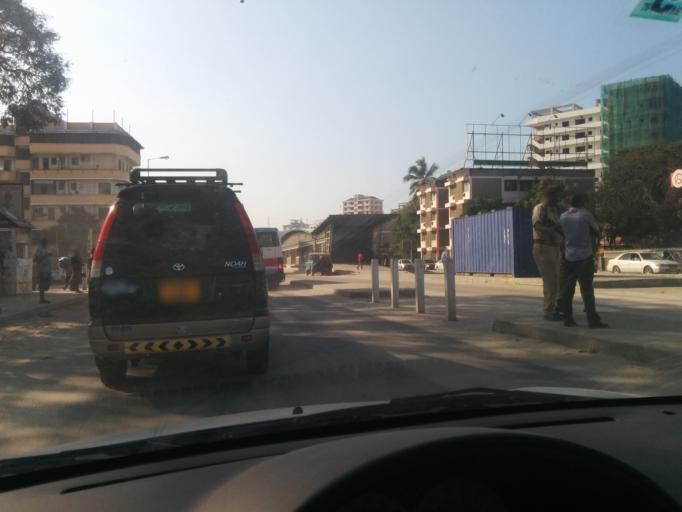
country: TZ
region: Dar es Salaam
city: Dar es Salaam
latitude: -6.8128
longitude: 39.2734
